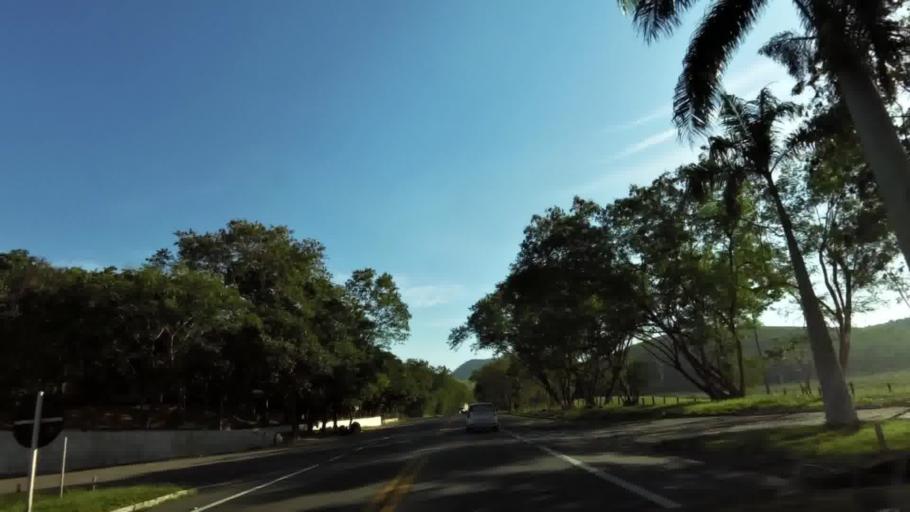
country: BR
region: Espirito Santo
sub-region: Viana
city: Viana
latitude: -20.4099
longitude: -40.4588
